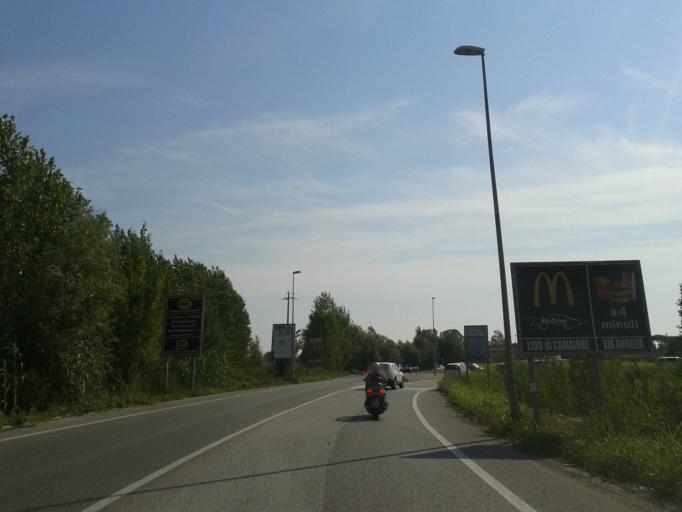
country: IT
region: Tuscany
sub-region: Provincia di Lucca
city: Camaiore
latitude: 43.8950
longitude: 10.2524
